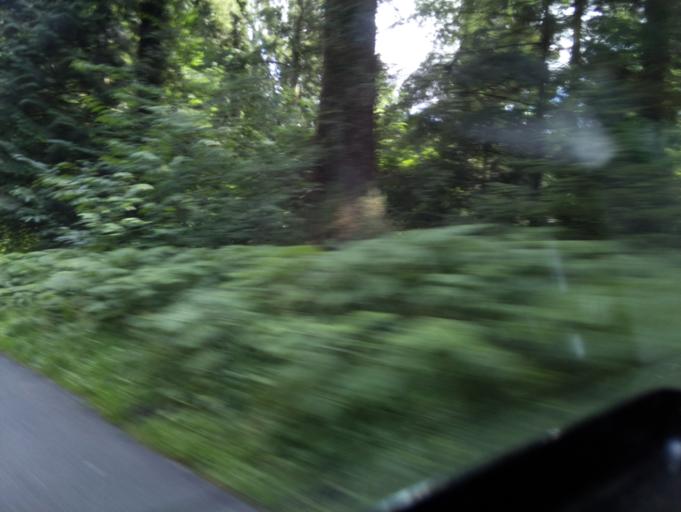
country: GB
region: England
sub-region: Gloucestershire
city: Cinderford
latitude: 51.7981
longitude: -2.4935
